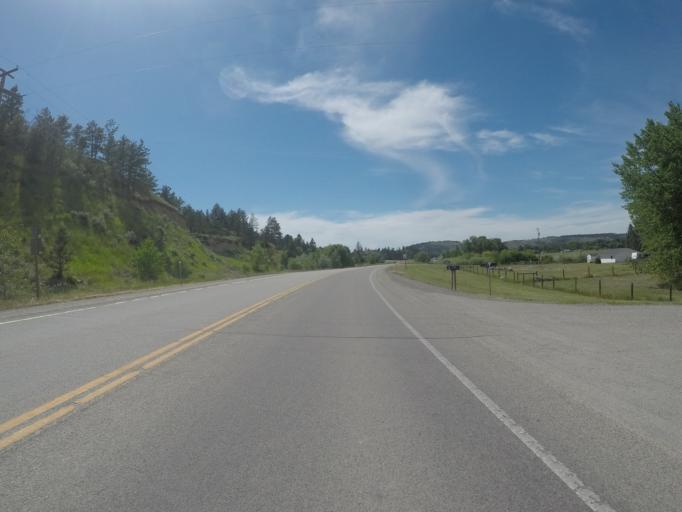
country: US
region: Montana
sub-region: Stillwater County
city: Columbus
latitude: 45.6269
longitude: -109.2602
